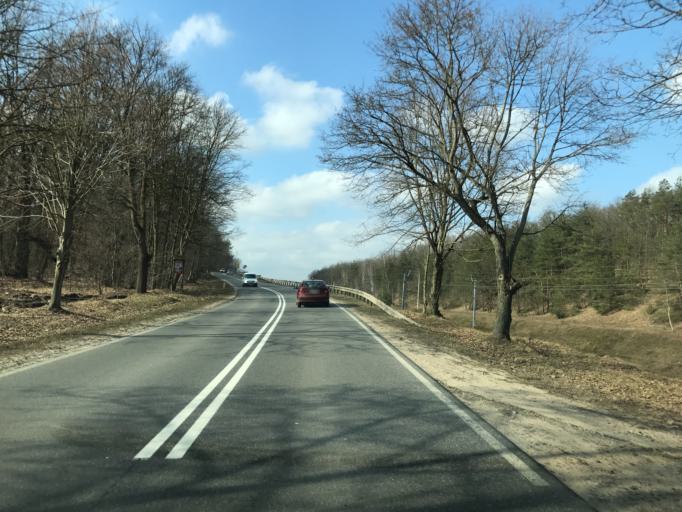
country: PL
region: Warmian-Masurian Voivodeship
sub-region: Powiat dzialdowski
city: Ilowo -Osada
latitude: 53.1563
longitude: 20.3155
